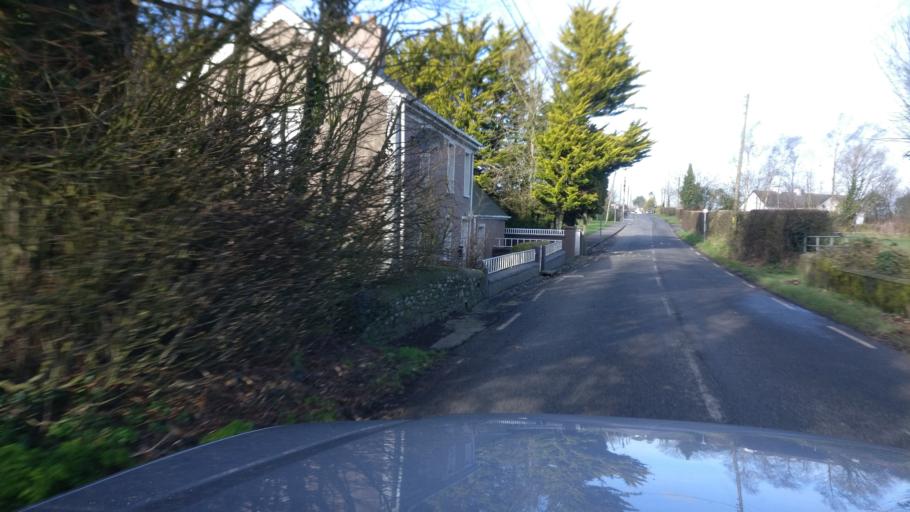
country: IE
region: Leinster
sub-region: Kilkenny
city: Castlecomer
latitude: 52.8664
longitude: -7.1649
